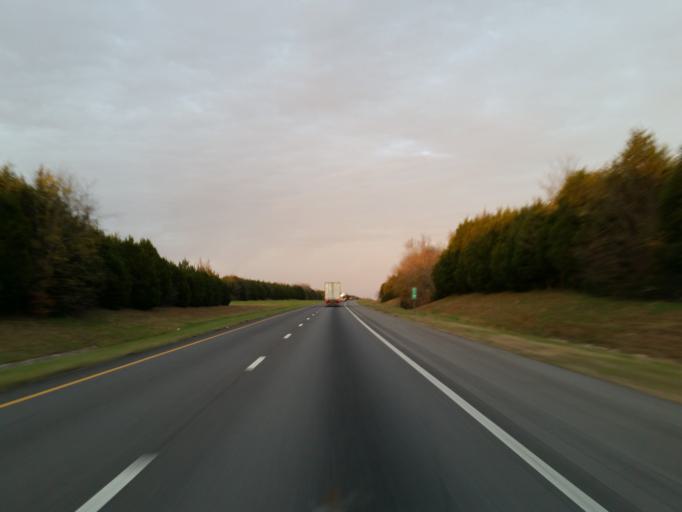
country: US
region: Alabama
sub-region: Sumter County
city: Livingston
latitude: 32.6496
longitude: -88.1920
